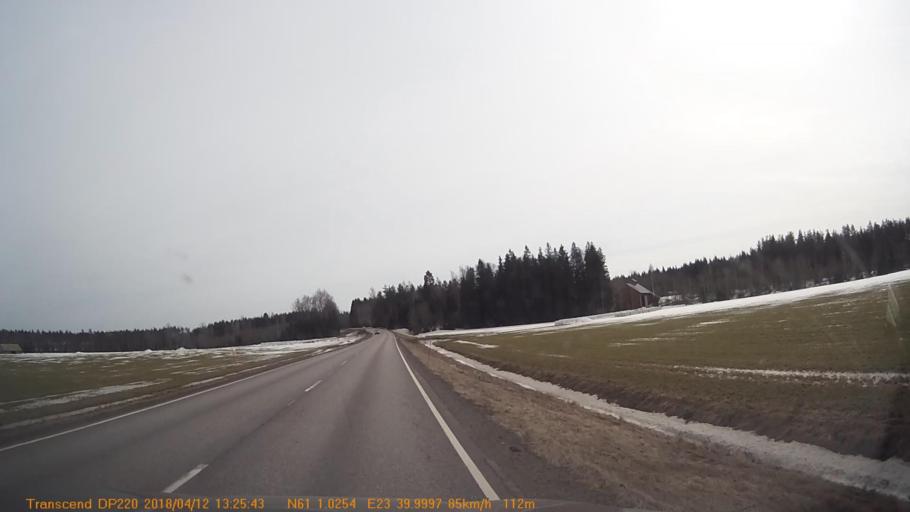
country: FI
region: Pirkanmaa
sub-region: Etelae-Pirkanmaa
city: Kylmaekoski
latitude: 61.0170
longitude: 23.6668
